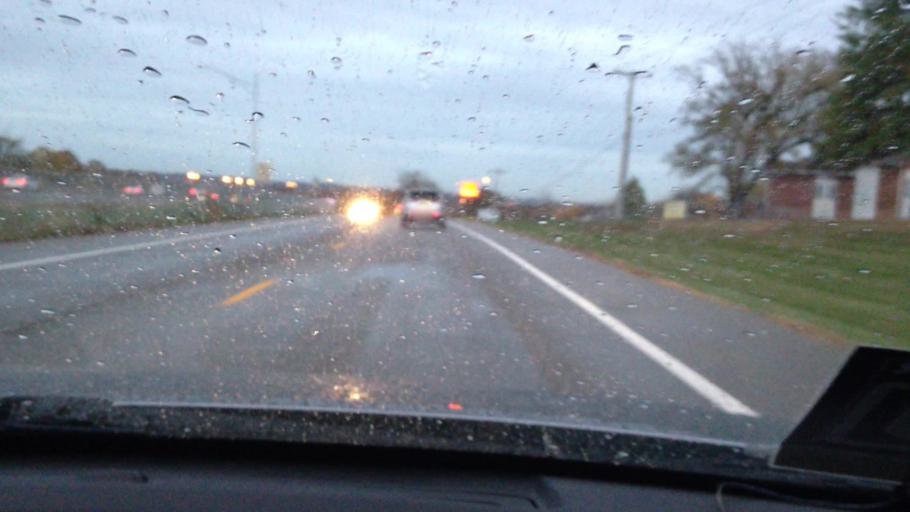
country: US
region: Missouri
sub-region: Platte County
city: Riverside
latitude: 39.2066
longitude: -94.6358
